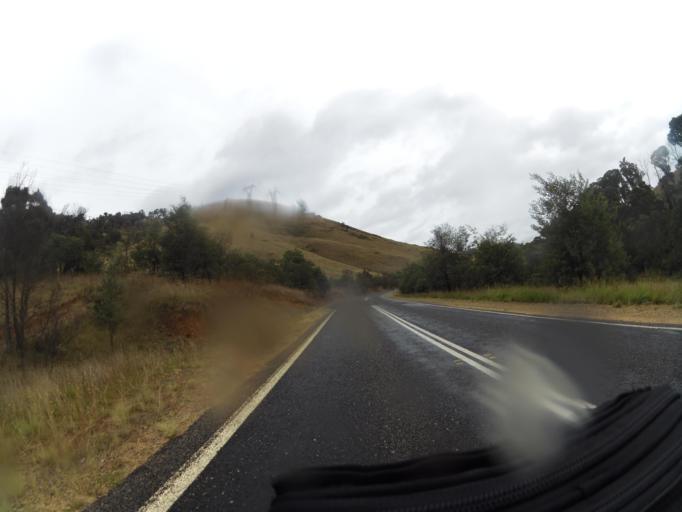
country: AU
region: New South Wales
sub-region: Greater Hume Shire
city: Holbrook
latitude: -36.2235
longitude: 147.6693
